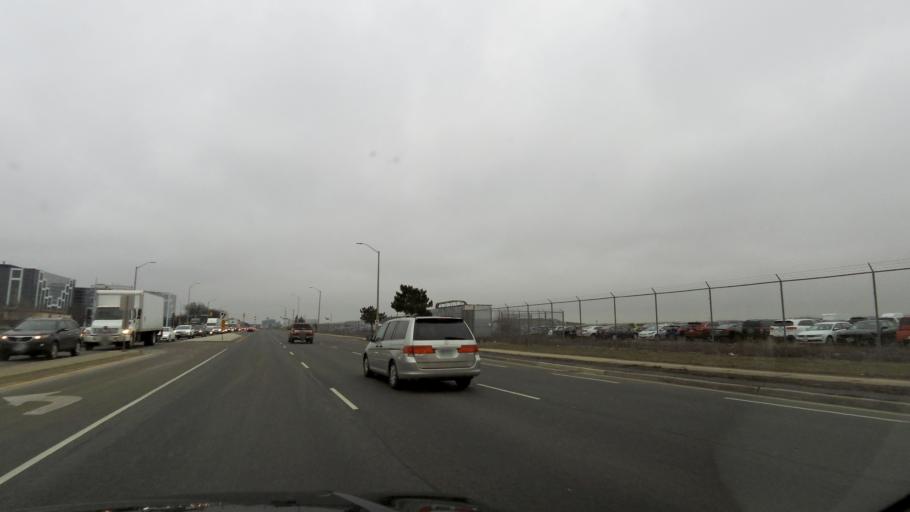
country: CA
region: Ontario
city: Etobicoke
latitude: 43.7005
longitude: -79.6377
